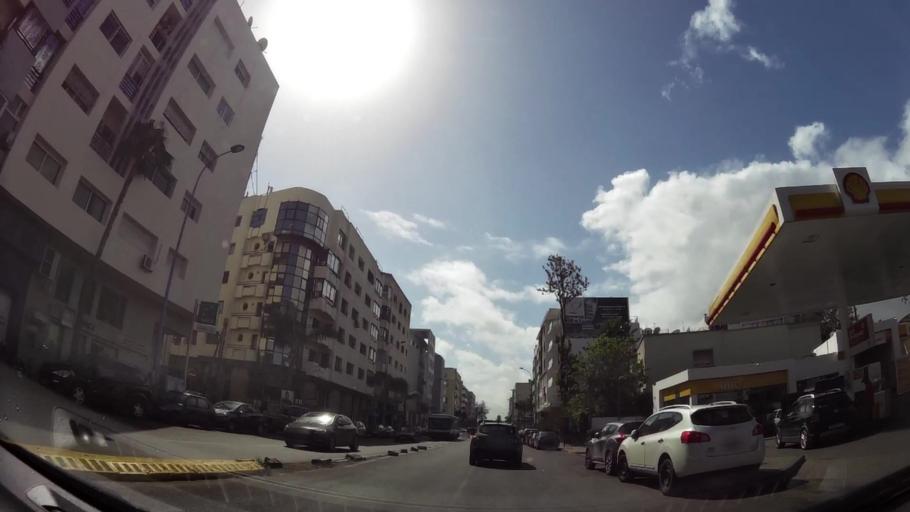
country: MA
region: Grand Casablanca
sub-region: Casablanca
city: Casablanca
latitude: 33.5736
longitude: -7.6148
